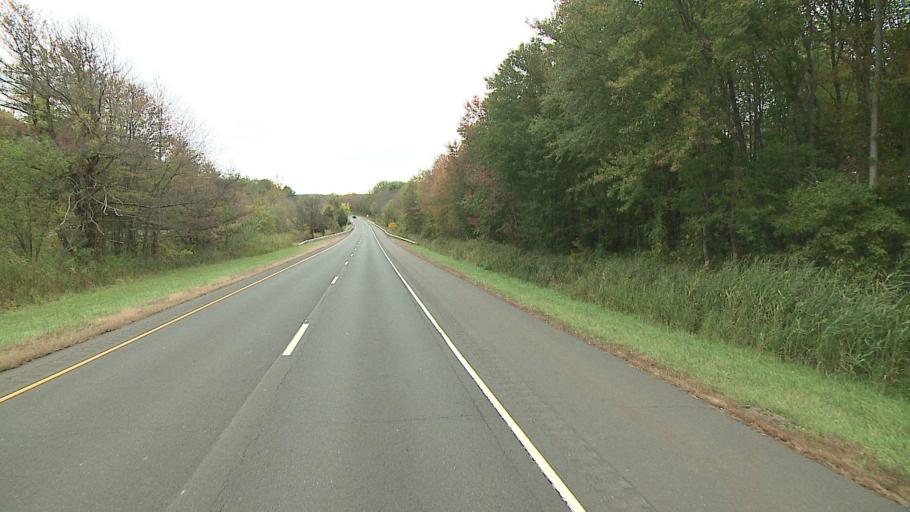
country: US
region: Connecticut
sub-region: Middlesex County
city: Higganum
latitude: 41.4912
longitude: -72.5673
